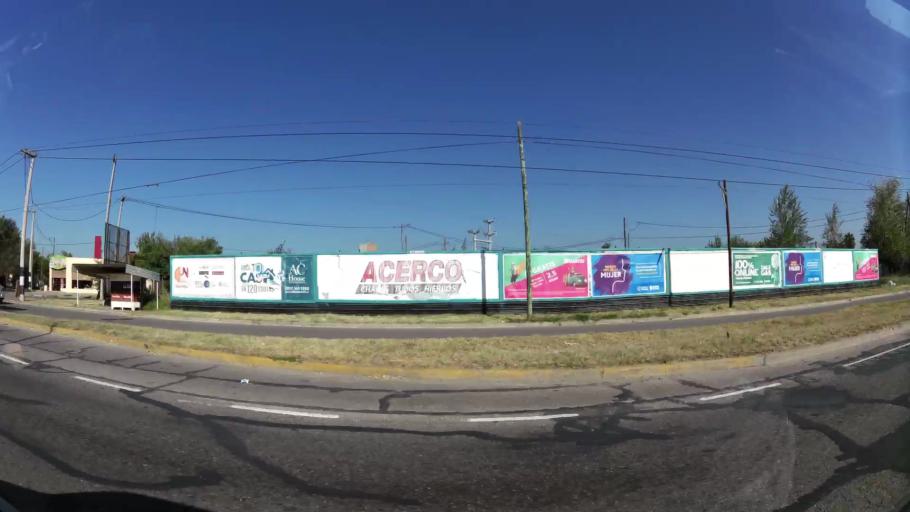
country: AR
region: Cordoba
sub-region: Departamento de Capital
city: Cordoba
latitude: -31.4736
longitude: -64.2321
